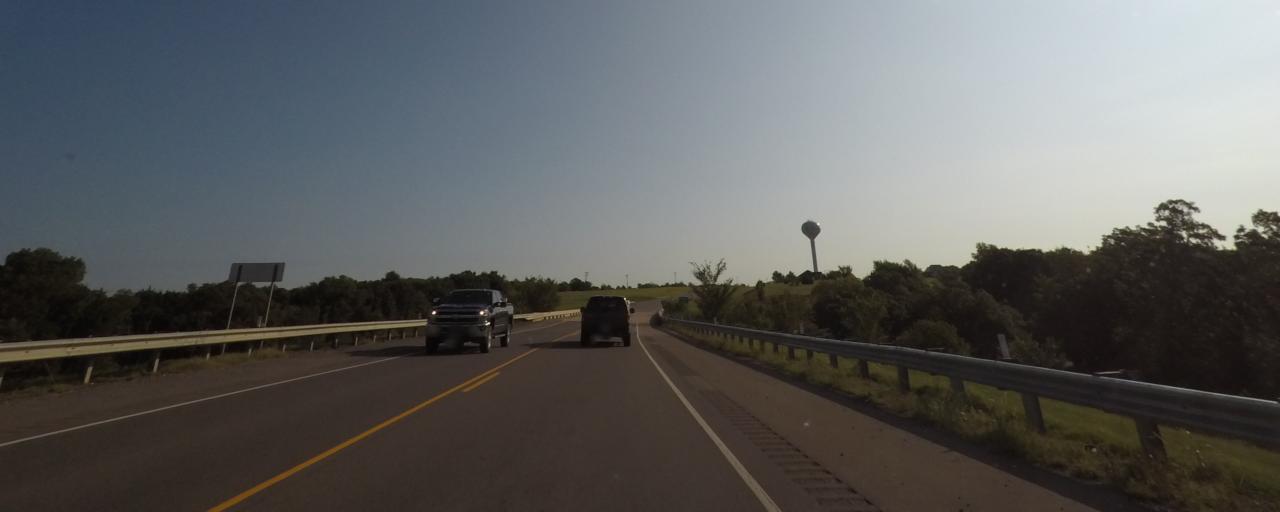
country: US
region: Oklahoma
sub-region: McClain County
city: Blanchard
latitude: 35.1208
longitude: -97.7044
